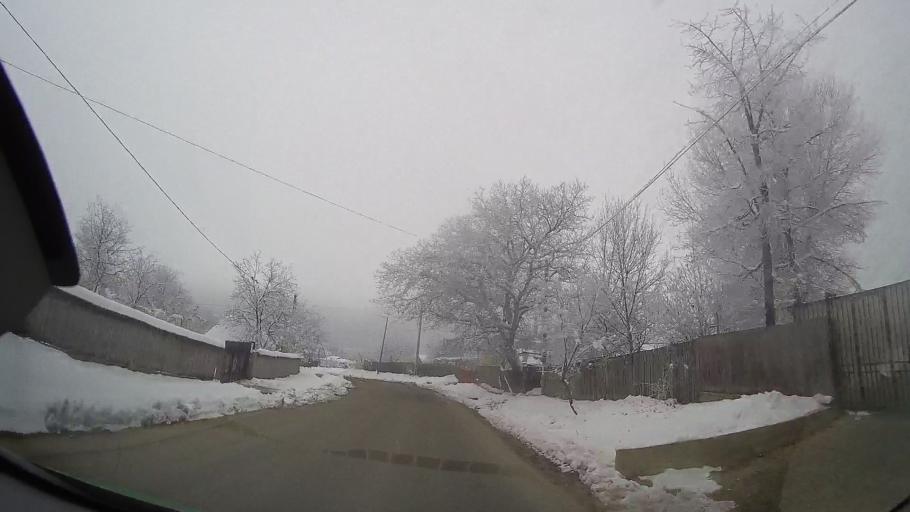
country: RO
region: Neamt
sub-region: Comuna Poenari
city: Poienari
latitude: 46.8879
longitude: 27.1325
